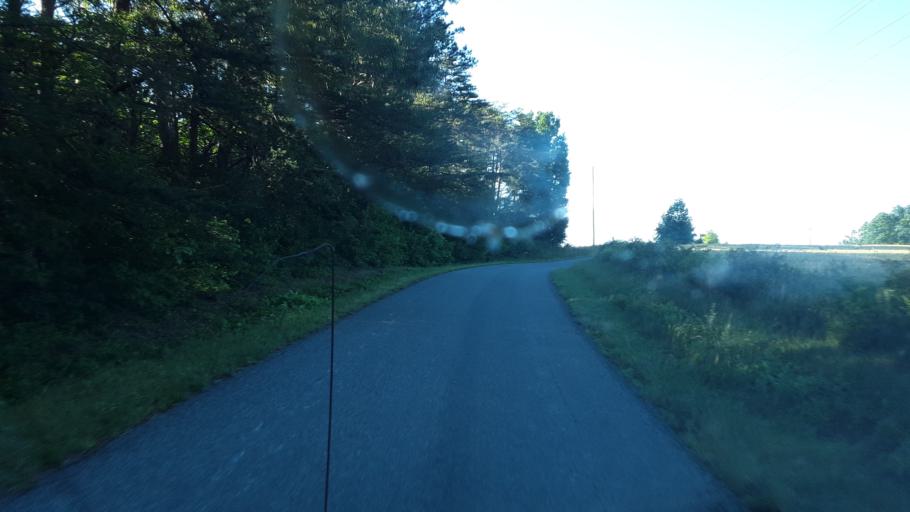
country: US
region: Virginia
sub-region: Pittsylvania County
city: Chatham
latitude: 36.8436
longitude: -79.4468
